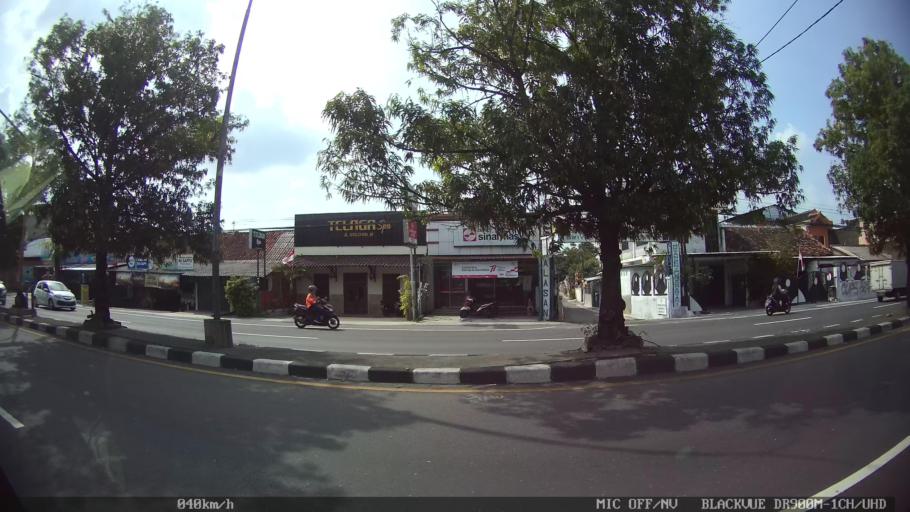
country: ID
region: Daerah Istimewa Yogyakarta
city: Depok
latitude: -7.7832
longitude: 110.4461
